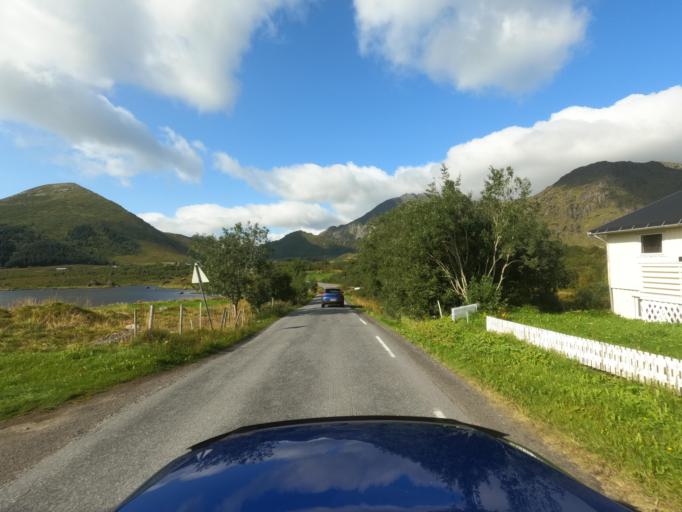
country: NO
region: Nordland
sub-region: Vestvagoy
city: Leknes
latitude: 68.1849
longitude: 13.6119
